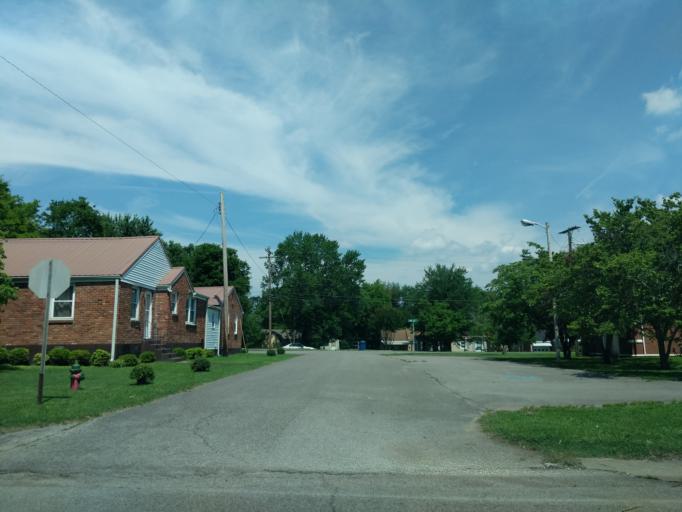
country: US
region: Tennessee
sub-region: Davidson County
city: Lakewood
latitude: 36.2556
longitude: -86.6479
